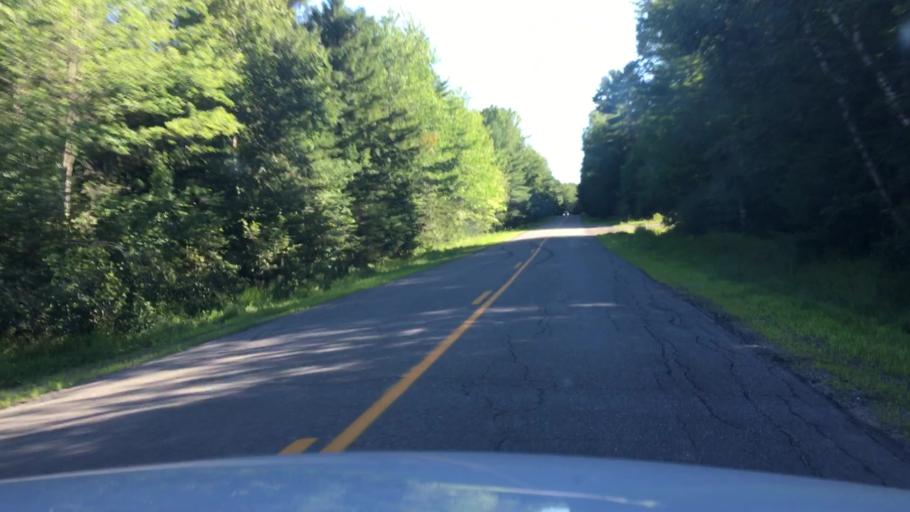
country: US
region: Maine
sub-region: Penobscot County
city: Enfield
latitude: 45.2155
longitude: -68.5855
